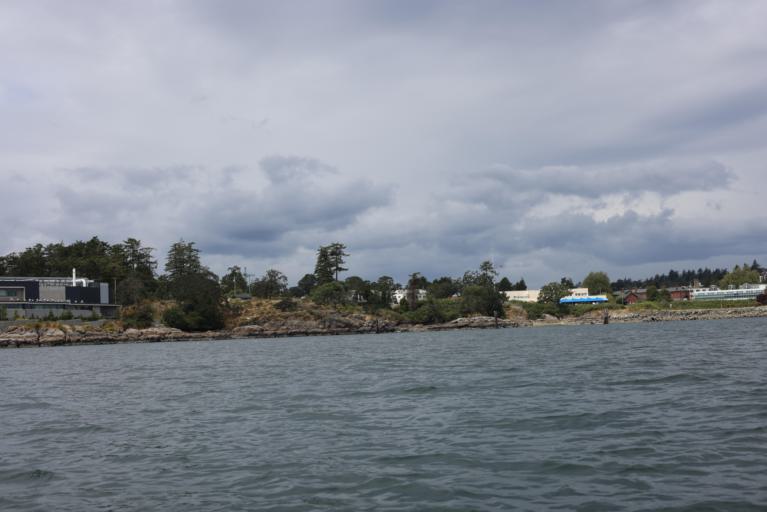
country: CA
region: British Columbia
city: Victoria
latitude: 48.4204
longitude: -123.3926
